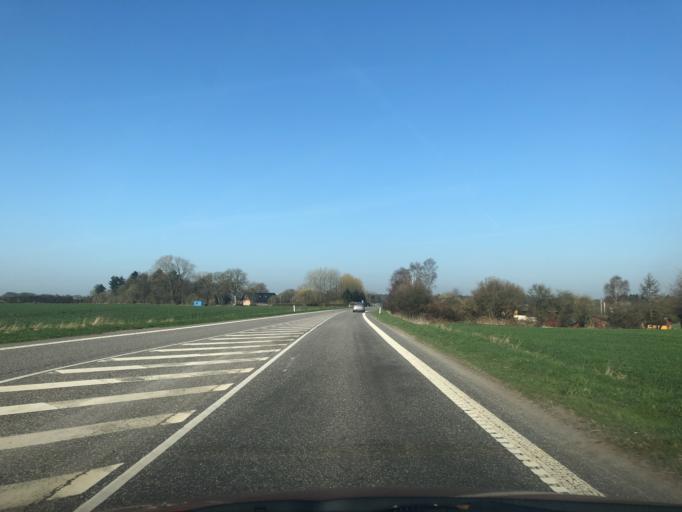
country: DK
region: Zealand
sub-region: Faxe Kommune
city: Fakse
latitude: 55.2705
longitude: 12.1315
